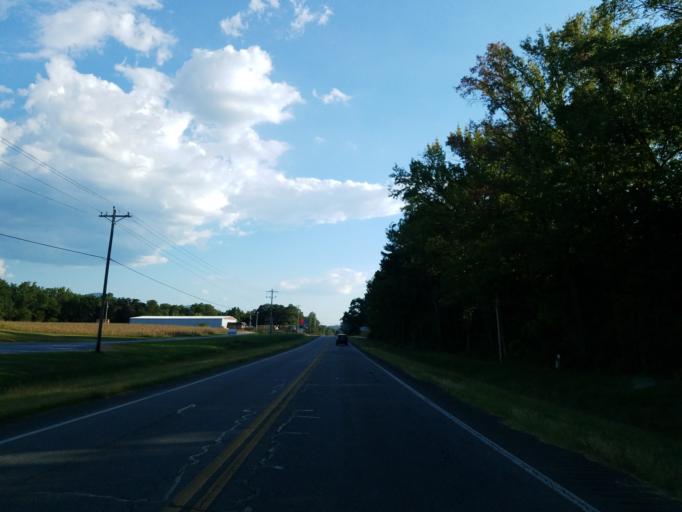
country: US
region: Georgia
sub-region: Murray County
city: Chatsworth
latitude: 34.8651
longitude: -84.7531
